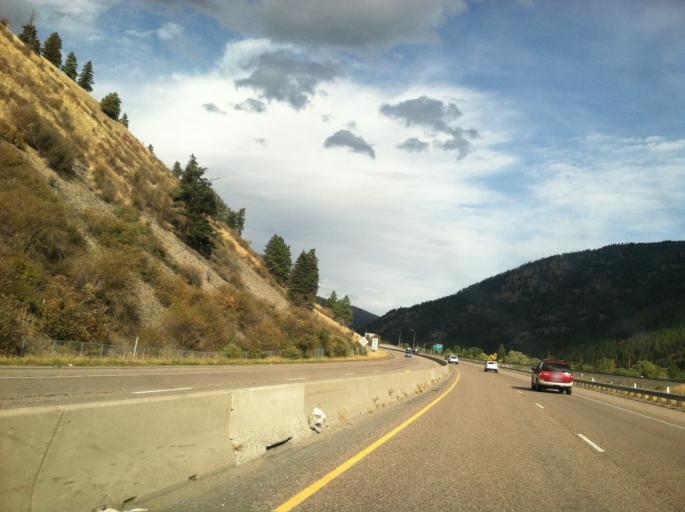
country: US
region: Montana
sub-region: Missoula County
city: East Missoula
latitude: 46.8638
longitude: -113.9626
